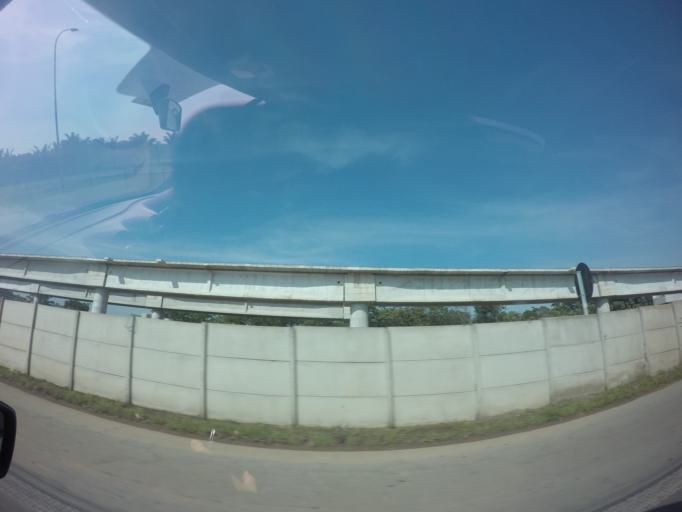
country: BR
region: Sao Paulo
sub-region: Guarulhos
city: Guarulhos
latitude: -23.4449
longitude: -46.4945
